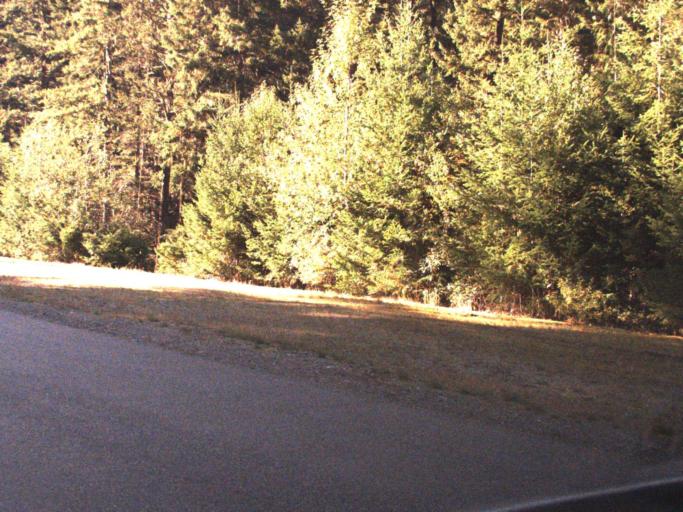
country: US
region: Washington
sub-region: Snohomish County
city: Darrington
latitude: 48.7060
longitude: -120.9242
